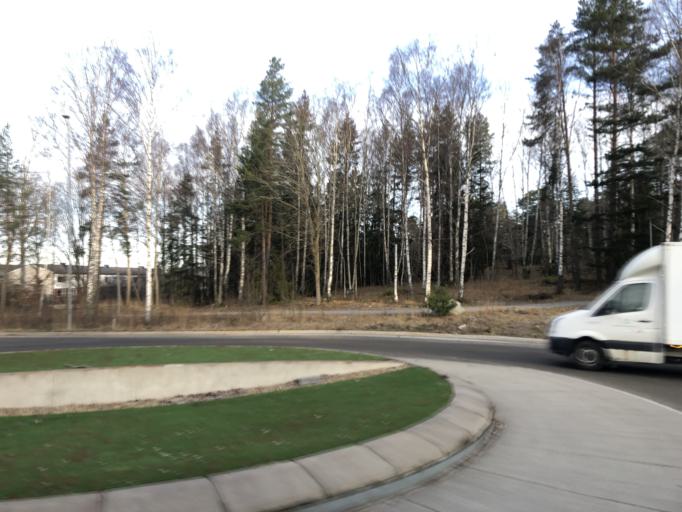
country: SE
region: Stockholm
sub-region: Jarfalla Kommun
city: Jakobsberg
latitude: 59.4024
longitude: 17.8029
